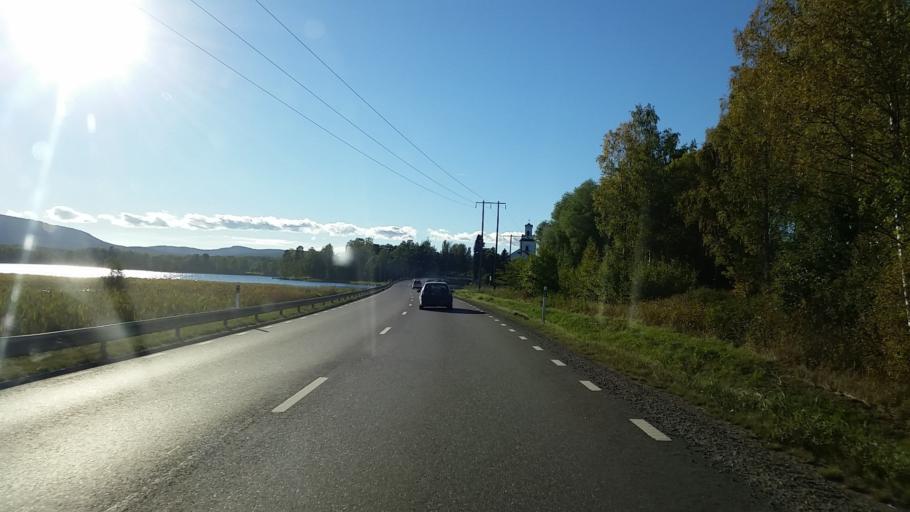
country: SE
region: Gaevleborg
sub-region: Hudiksvalls Kommun
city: Sorforsa
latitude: 61.7337
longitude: 16.9488
